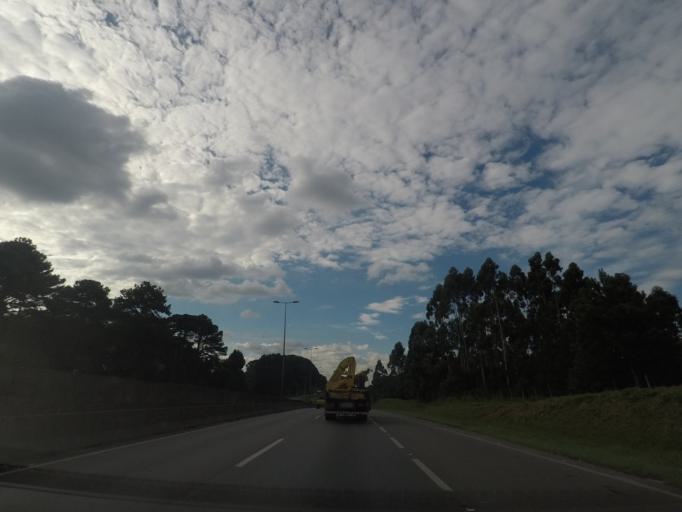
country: BR
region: Parana
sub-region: Araucaria
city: Araucaria
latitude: -25.5780
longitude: -49.3125
